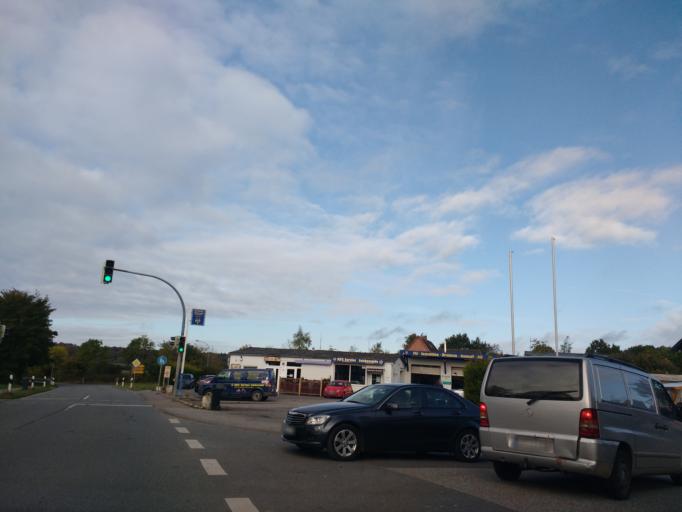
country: DE
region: Schleswig-Holstein
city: Schonwalde am Bungsberg
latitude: 54.1900
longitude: 10.7550
